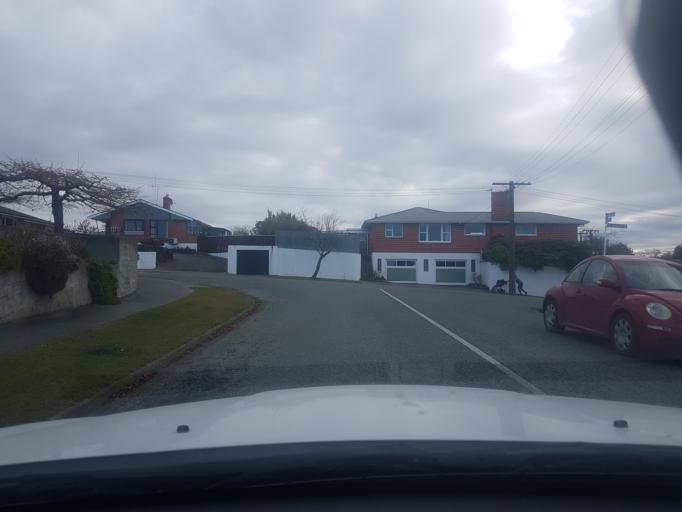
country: NZ
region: Canterbury
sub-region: Timaru District
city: Timaru
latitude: -44.3914
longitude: 171.2162
